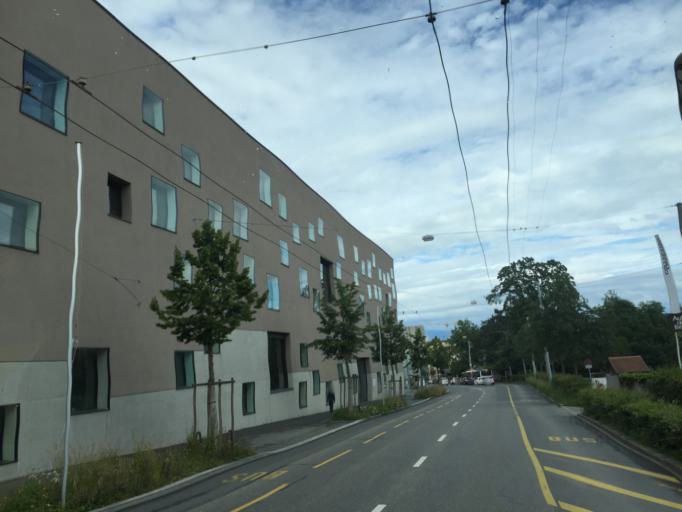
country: CH
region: Vaud
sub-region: Lausanne District
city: Blecherette
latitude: 46.5279
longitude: 6.6243
